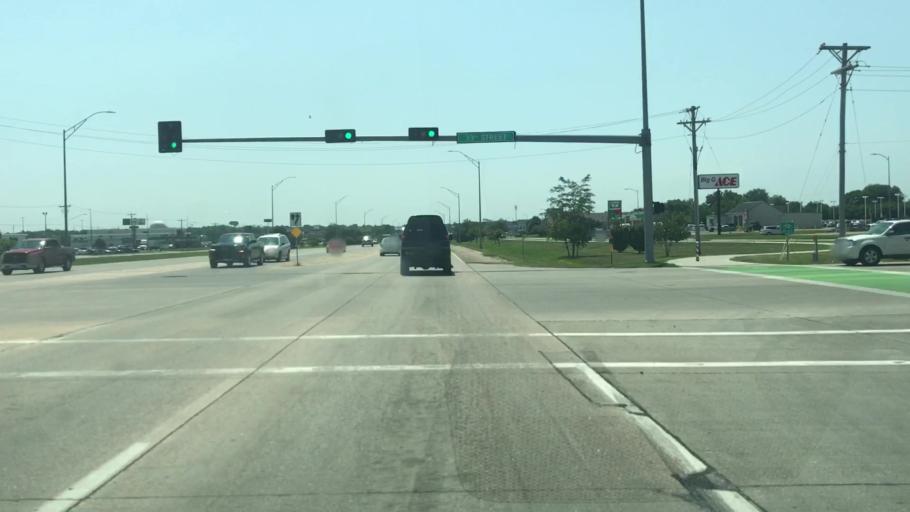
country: US
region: Nebraska
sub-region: Adams County
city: Hastings
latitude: 40.6190
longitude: -98.3831
